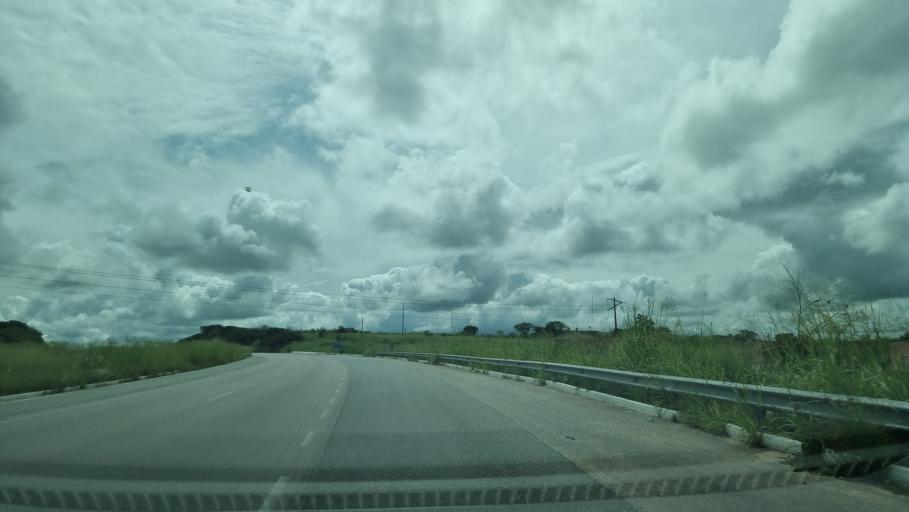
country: BR
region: Pernambuco
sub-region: Caruaru
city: Caruaru
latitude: -8.3304
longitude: -35.9824
